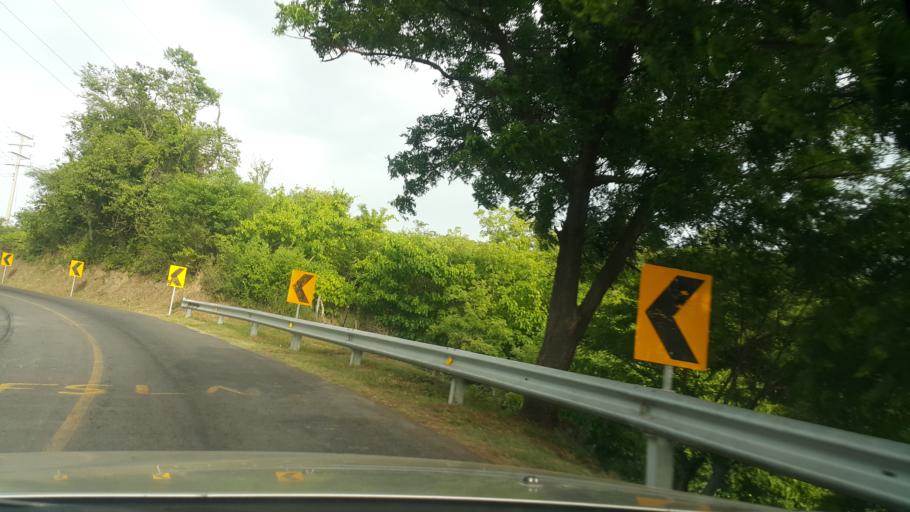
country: NI
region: Managua
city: Masachapa
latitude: 11.8150
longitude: -86.4771
